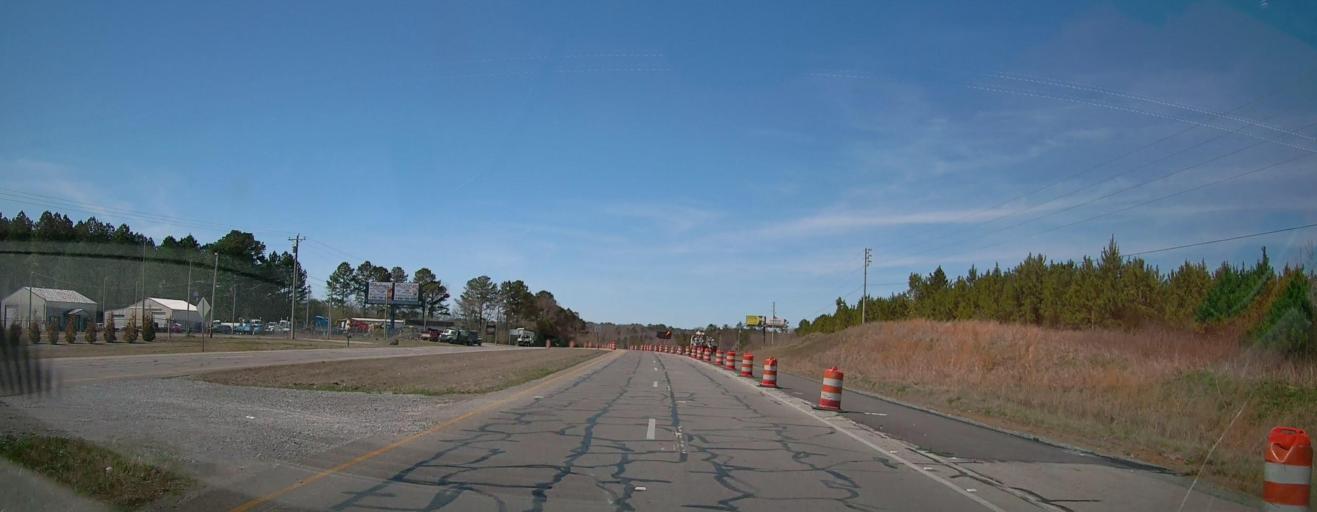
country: US
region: Alabama
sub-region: Cullman County
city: Cullman
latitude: 34.1939
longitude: -86.7875
